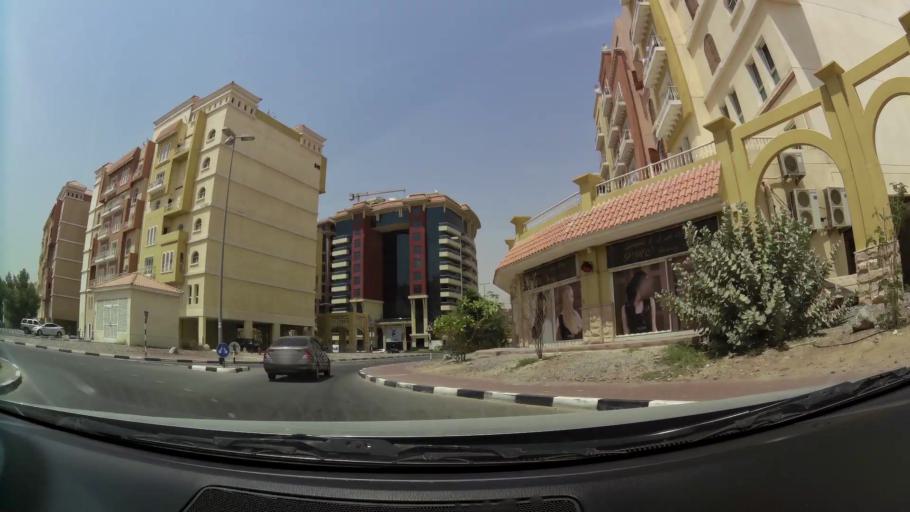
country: AE
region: Ash Shariqah
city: Sharjah
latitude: 25.1638
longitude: 55.4048
